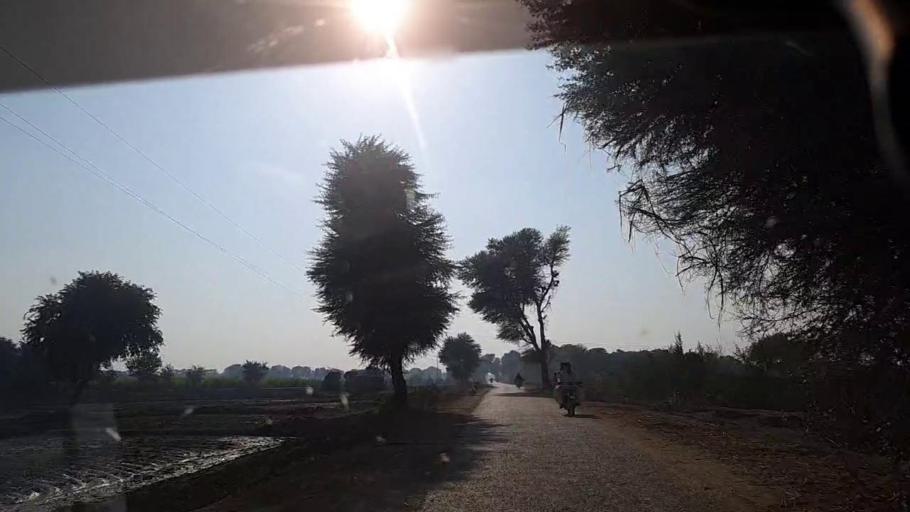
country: PK
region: Sindh
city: Sobhadero
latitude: 27.2495
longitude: 68.2953
